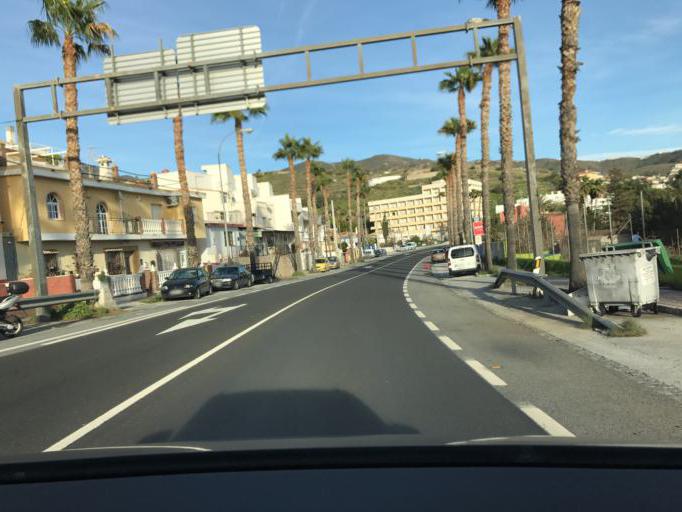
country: ES
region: Andalusia
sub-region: Provincia de Granada
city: Almunecar
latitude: 36.7490
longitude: -3.6650
